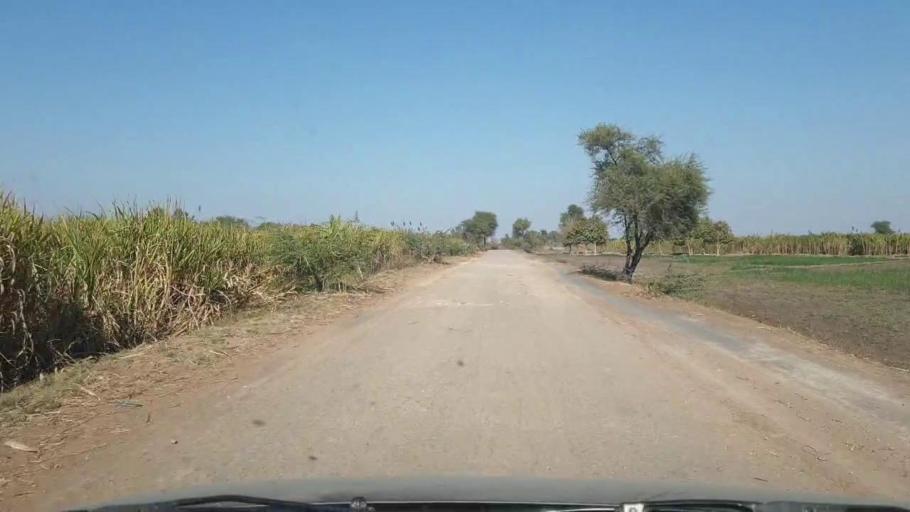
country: PK
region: Sindh
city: Samaro
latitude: 25.3690
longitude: 69.3246
